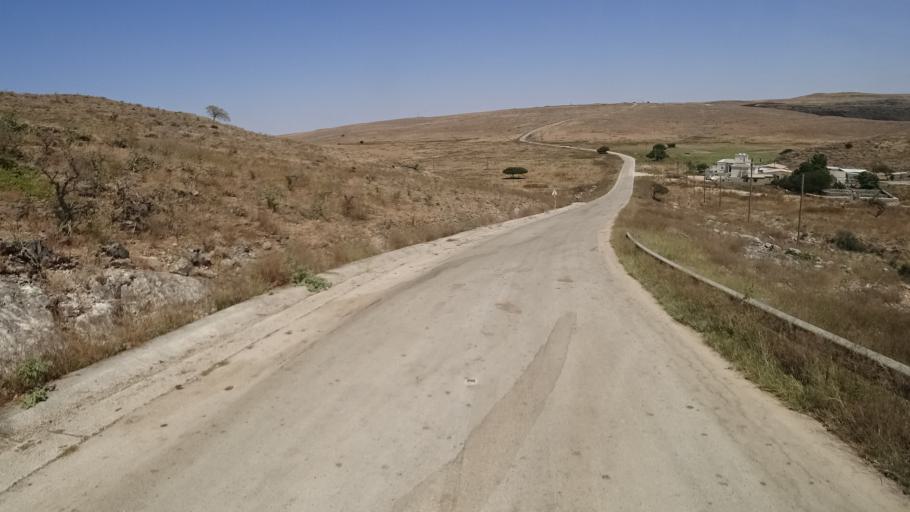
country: OM
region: Zufar
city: Salalah
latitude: 17.1498
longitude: 54.6176
